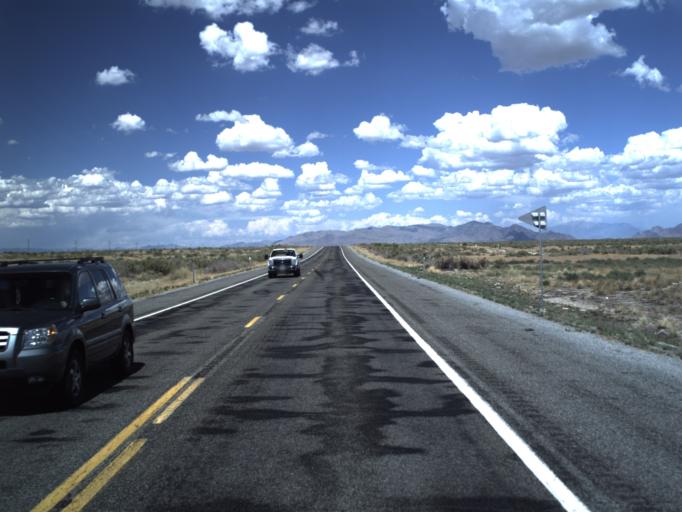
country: US
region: Utah
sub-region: Millard County
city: Delta
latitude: 39.4267
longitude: -112.4705
